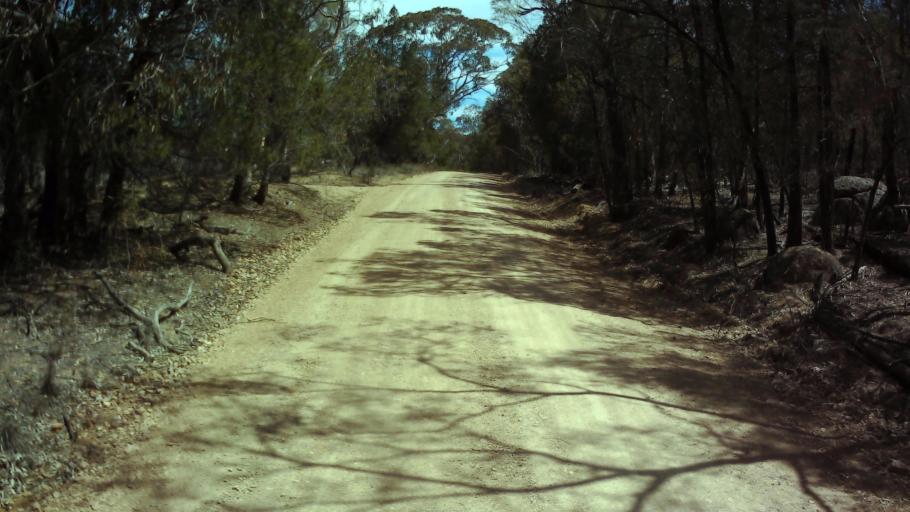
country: AU
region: New South Wales
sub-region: Weddin
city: Grenfell
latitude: -33.8082
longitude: 148.1596
